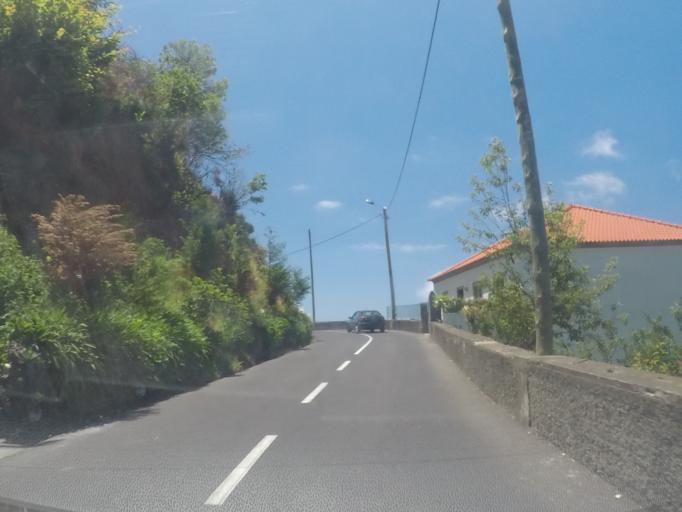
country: PT
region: Madeira
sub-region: Camara de Lobos
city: Curral das Freiras
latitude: 32.6827
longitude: -16.9910
